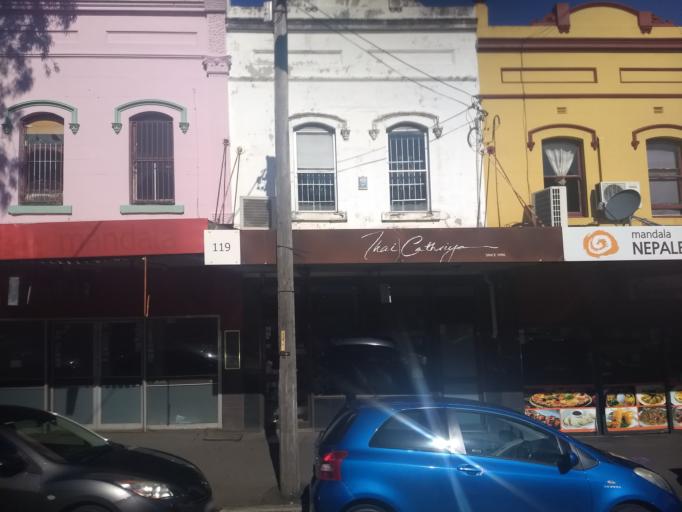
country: AU
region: New South Wales
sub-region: Randwick
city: Randwick
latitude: -33.9124
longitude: 151.2426
